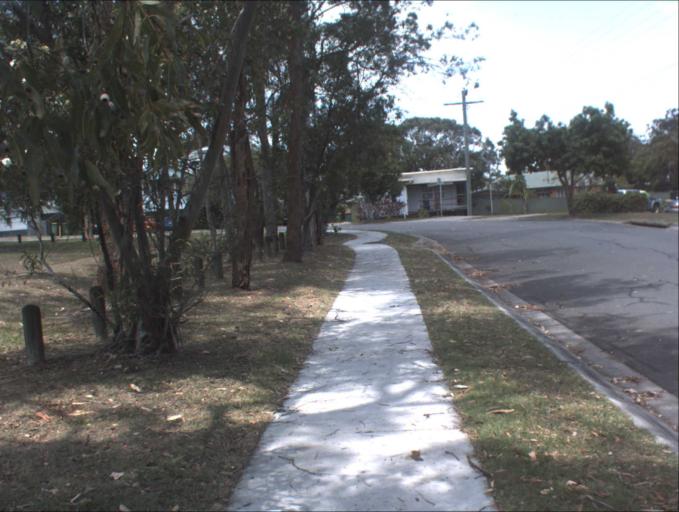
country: AU
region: Queensland
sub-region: Logan
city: Woodridge
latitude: -27.6354
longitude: 153.0958
